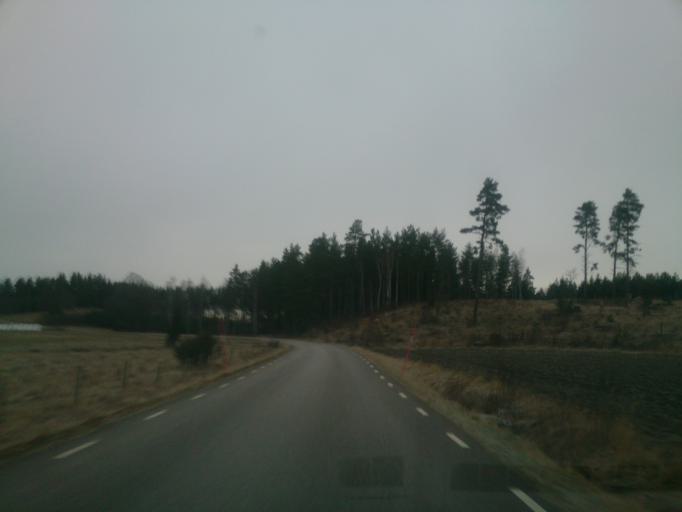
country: SE
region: OEstergoetland
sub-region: Norrkopings Kommun
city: Krokek
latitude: 58.5015
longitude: 16.5480
